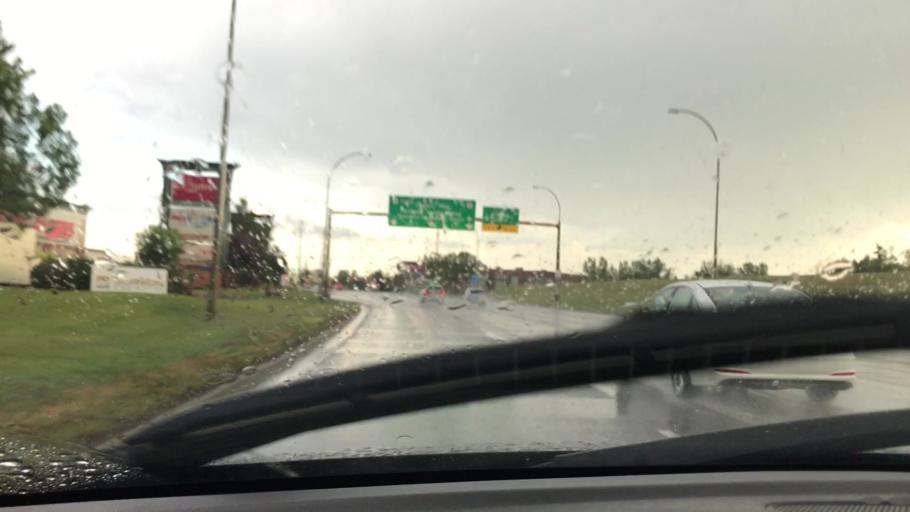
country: CA
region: Alberta
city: Edmonton
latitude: 53.4658
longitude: -113.4955
